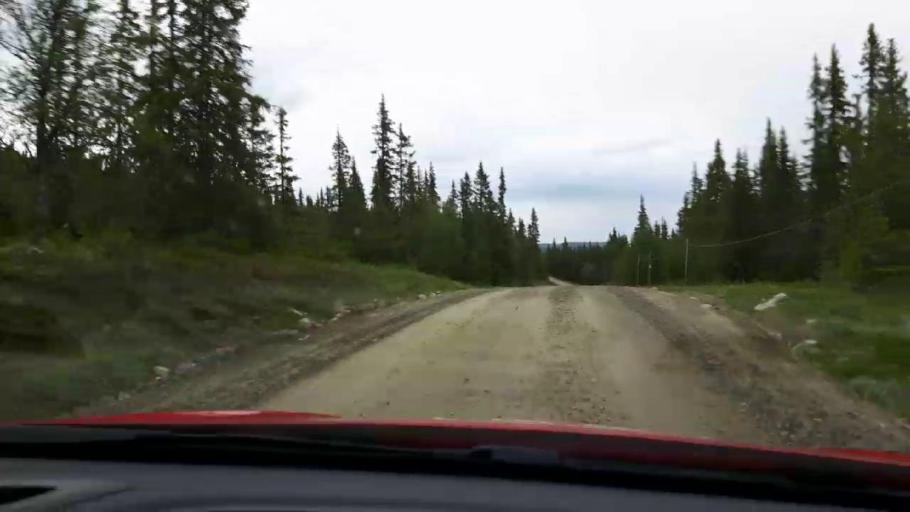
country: SE
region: Jaemtland
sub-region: Are Kommun
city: Are
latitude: 62.8257
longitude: 12.8120
